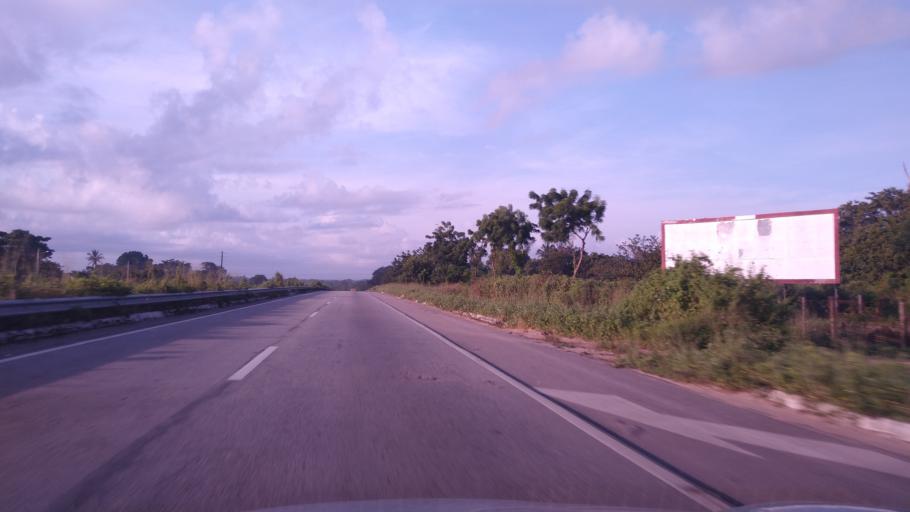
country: BR
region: Ceara
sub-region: Pacajus
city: Pacajus
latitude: -4.1752
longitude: -38.4927
